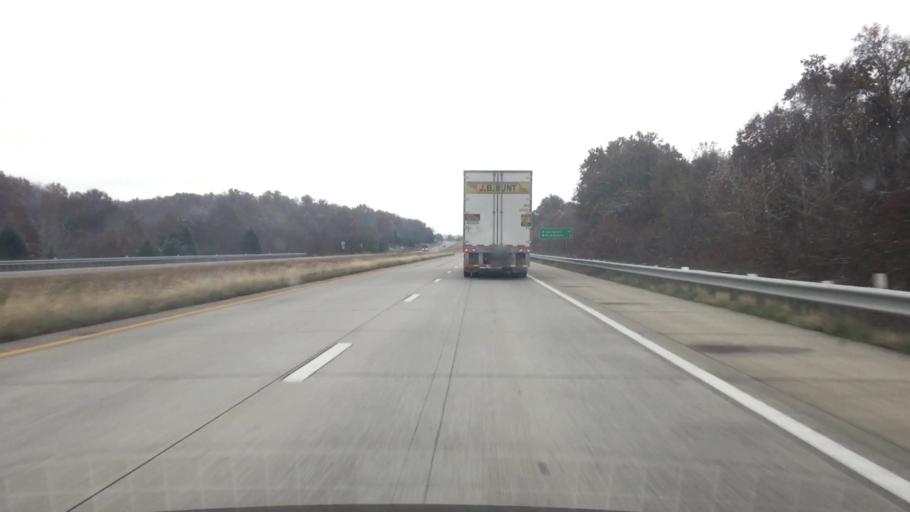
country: US
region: Missouri
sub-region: Henry County
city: Clinton
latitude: 38.2241
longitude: -93.7620
